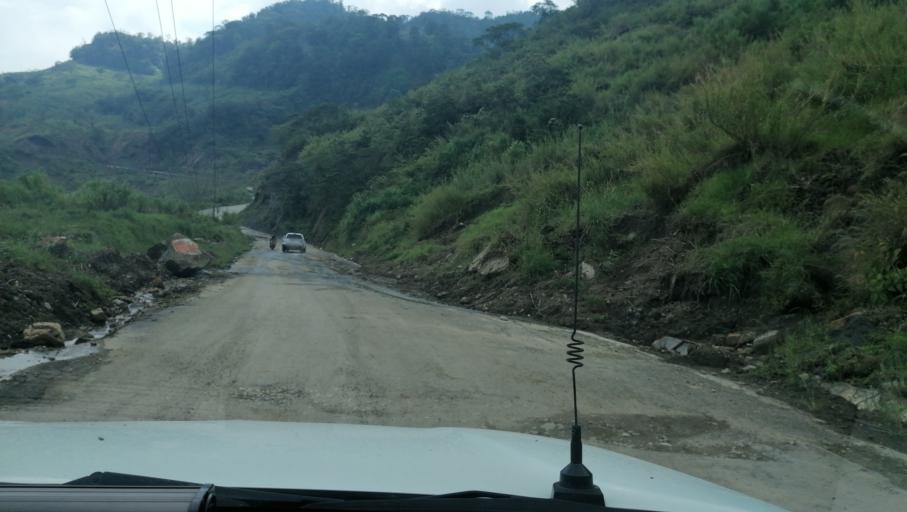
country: MX
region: Chiapas
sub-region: Ocotepec
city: San Pablo Huacano
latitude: 17.2635
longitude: -93.2666
